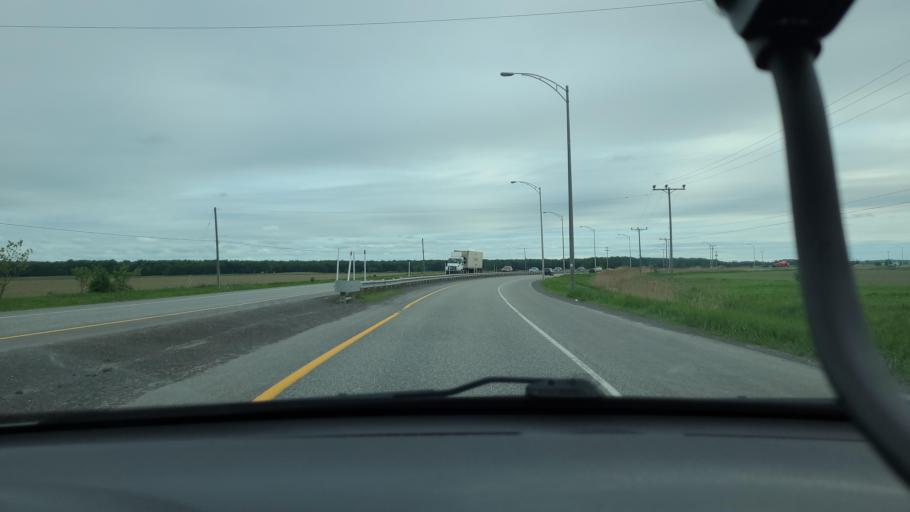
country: CA
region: Quebec
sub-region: Lanaudiere
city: Sainte-Julienne
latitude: 45.9086
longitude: -73.6581
